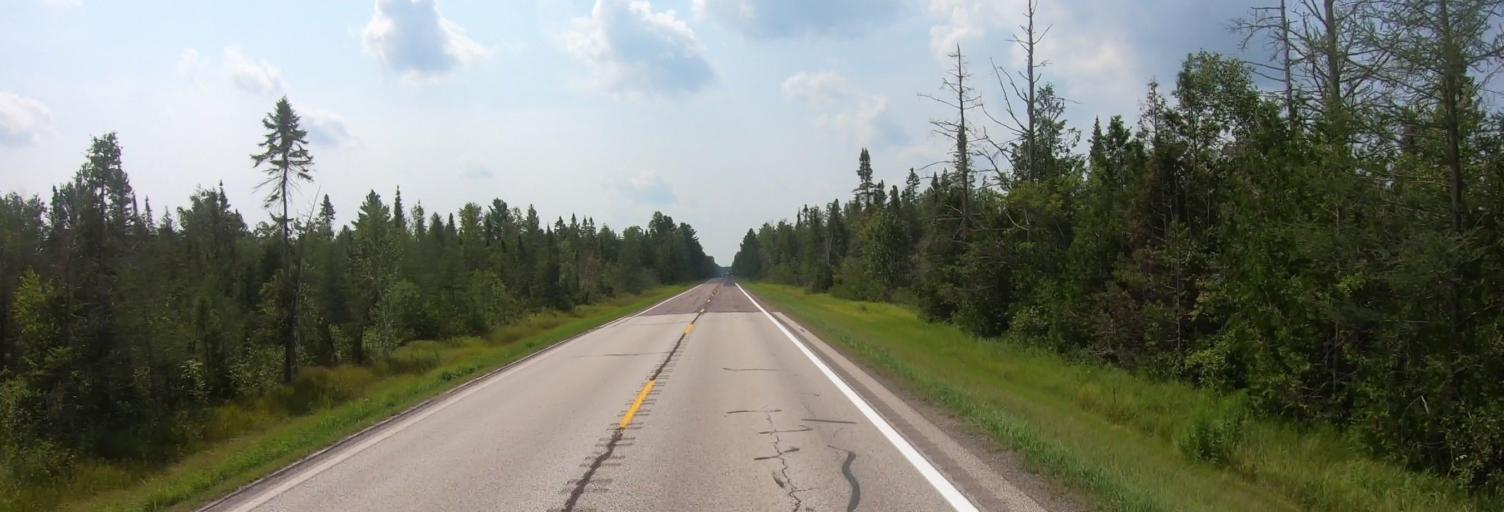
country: US
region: Michigan
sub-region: Luce County
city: Newberry
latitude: 46.4863
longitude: -85.4268
